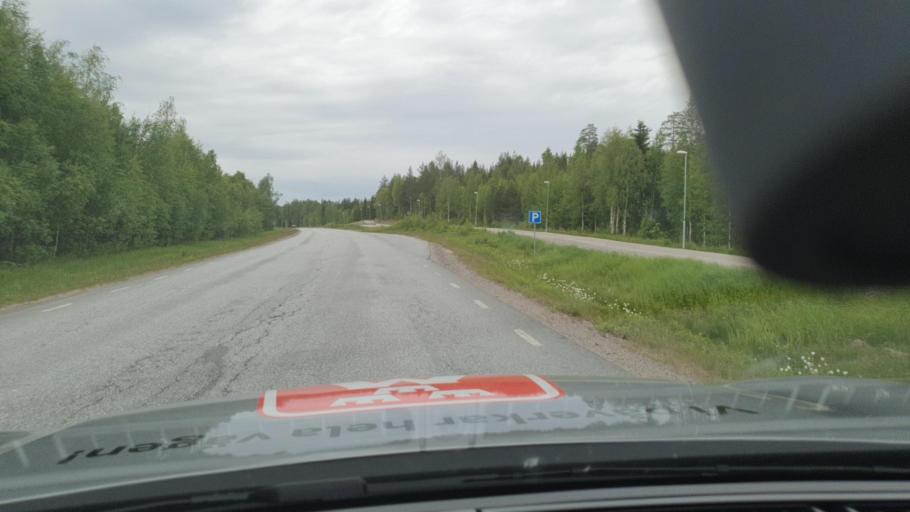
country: SE
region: Norrbotten
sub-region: Kalix Kommun
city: Rolfs
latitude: 65.8729
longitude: 23.1105
